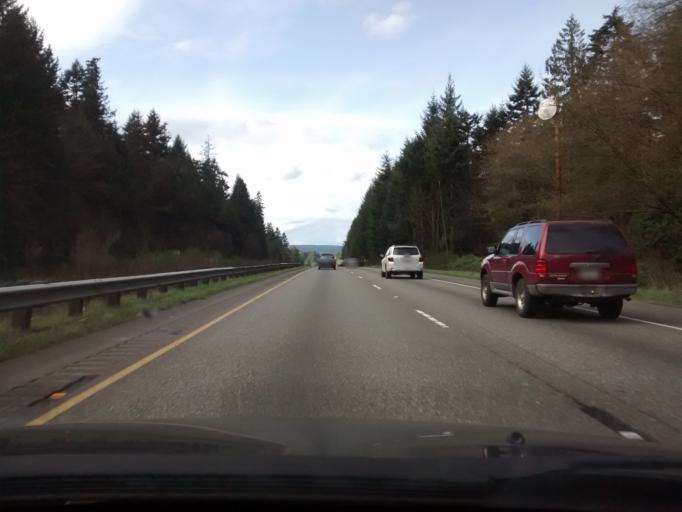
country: US
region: Washington
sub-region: Pierce County
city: Canterwood
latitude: 47.3487
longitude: -122.6101
